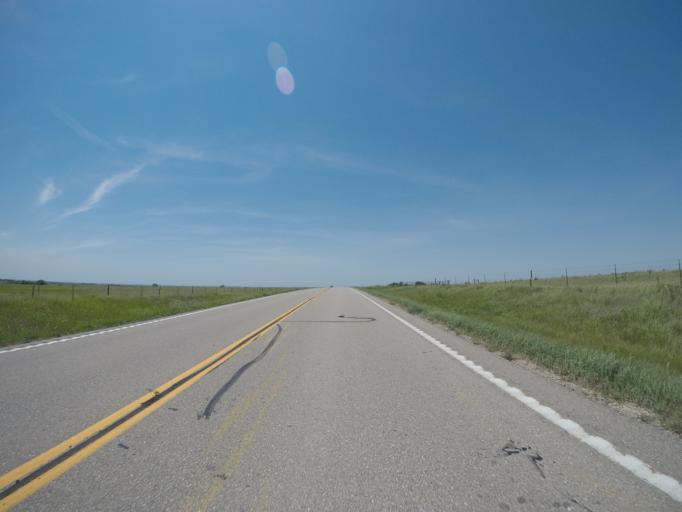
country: US
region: Kansas
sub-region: Dickinson County
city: Solomon
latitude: 39.0308
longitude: -97.4315
